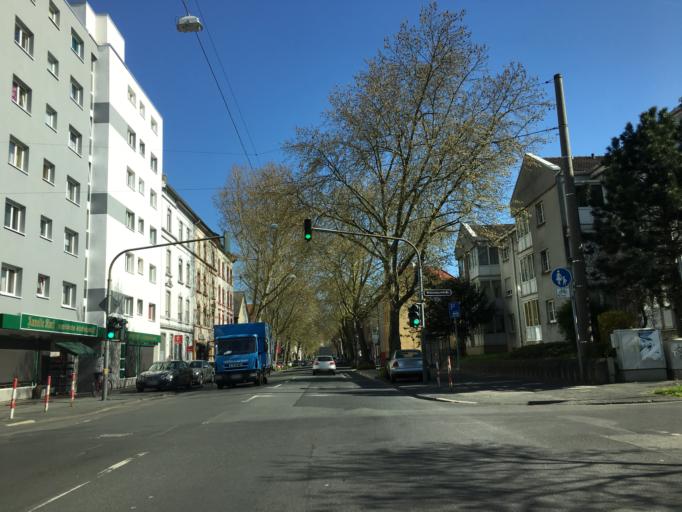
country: DE
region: Hesse
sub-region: Regierungsbezirk Darmstadt
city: Offenbach
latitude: 50.0930
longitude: 8.7522
